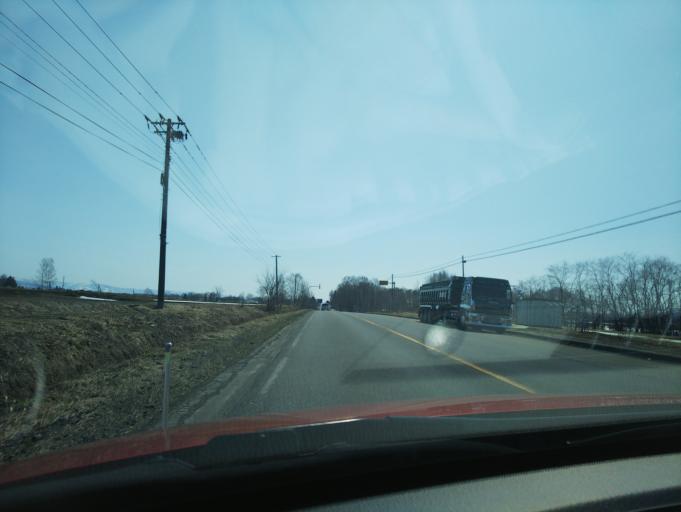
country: JP
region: Hokkaido
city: Nayoro
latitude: 44.2554
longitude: 142.3947
